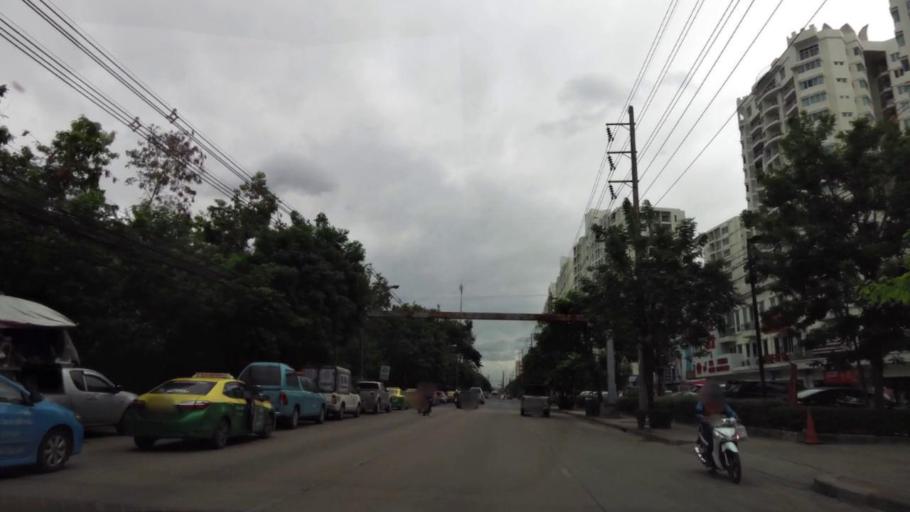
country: TH
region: Bangkok
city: Huai Khwang
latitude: 13.7670
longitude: 100.5794
